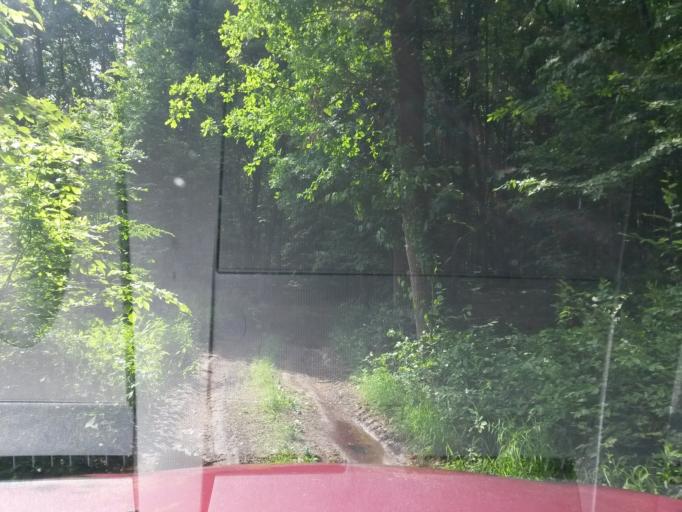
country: SK
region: Kosicky
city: Kosice
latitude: 48.7550
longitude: 21.2253
